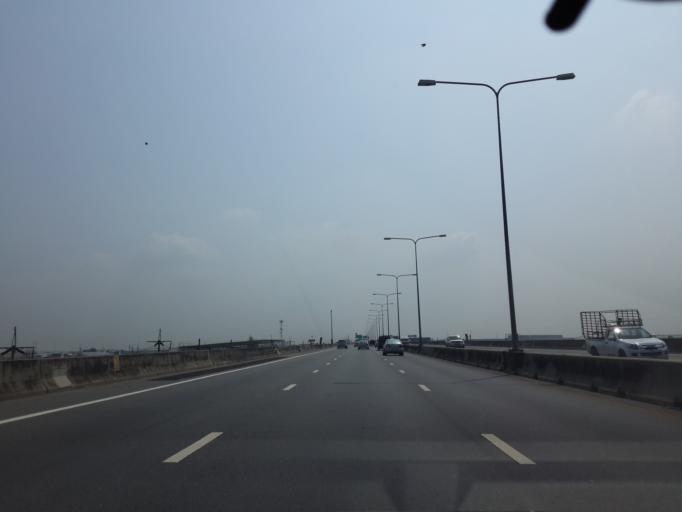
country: TH
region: Chachoengsao
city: Bang Pakong
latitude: 13.5708
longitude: 100.9183
